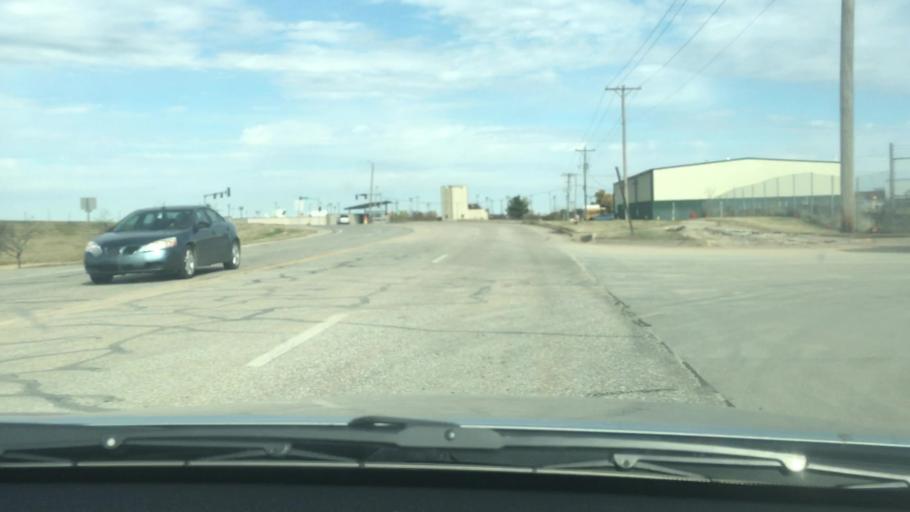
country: US
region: Kansas
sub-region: Sedgwick County
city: Wichita
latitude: 37.6337
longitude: -97.2857
